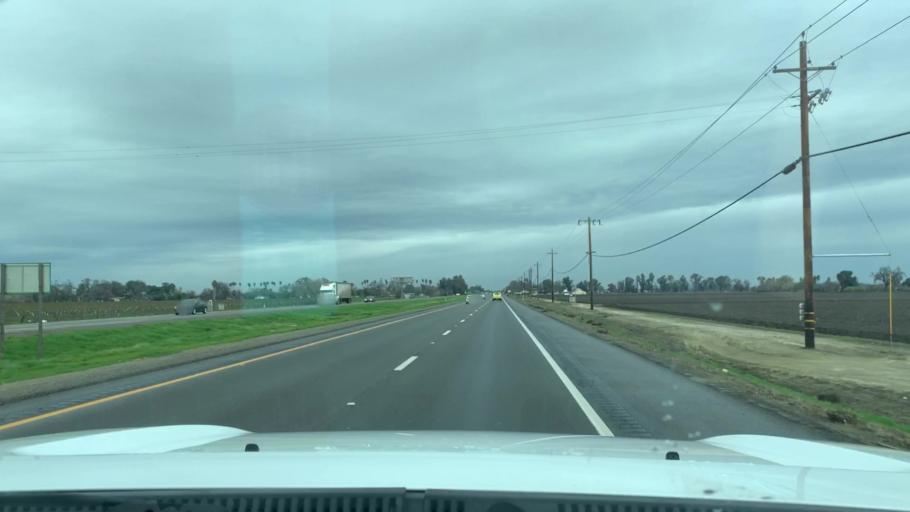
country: US
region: California
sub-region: Kings County
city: Lemoore
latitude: 36.3219
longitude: -119.8078
